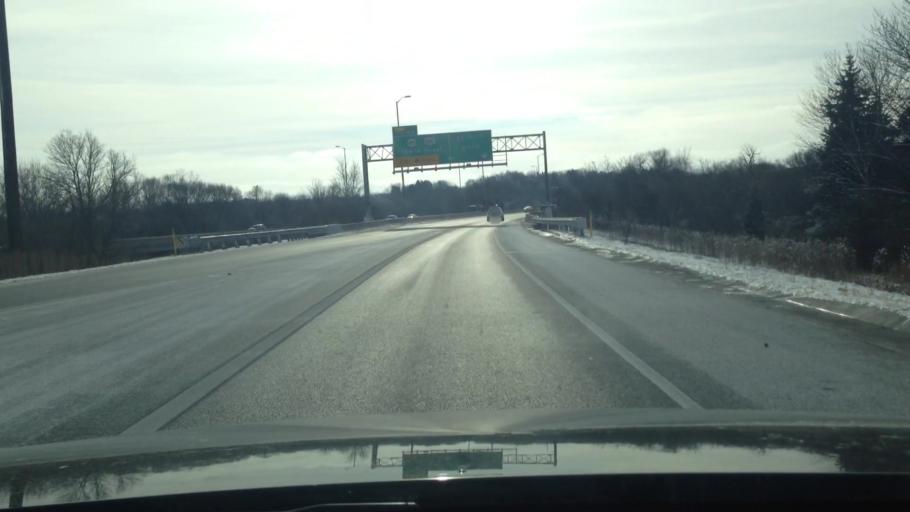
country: US
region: Wisconsin
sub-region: Milwaukee County
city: Hales Corners
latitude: 42.9621
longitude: -88.0396
